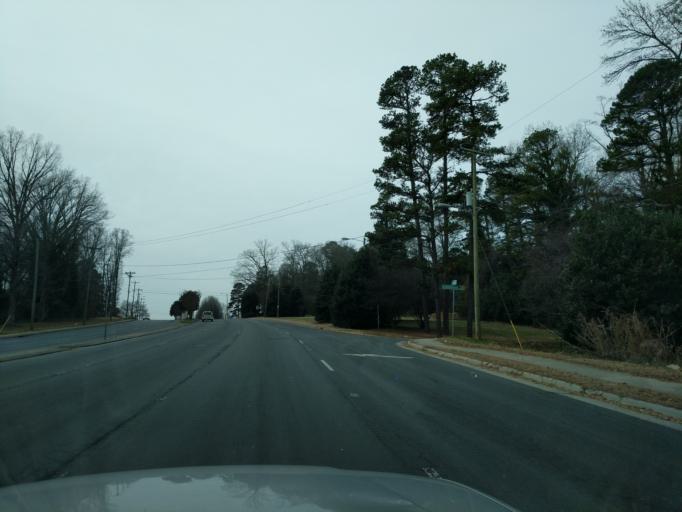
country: US
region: North Carolina
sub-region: Mecklenburg County
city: Charlotte
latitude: 35.1998
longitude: -80.7881
